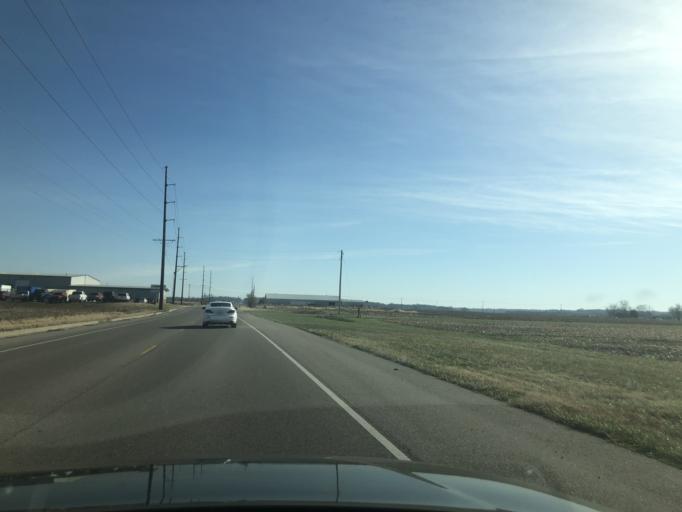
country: US
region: Indiana
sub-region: Warrick County
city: Newburgh
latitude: 37.9911
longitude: -87.4468
